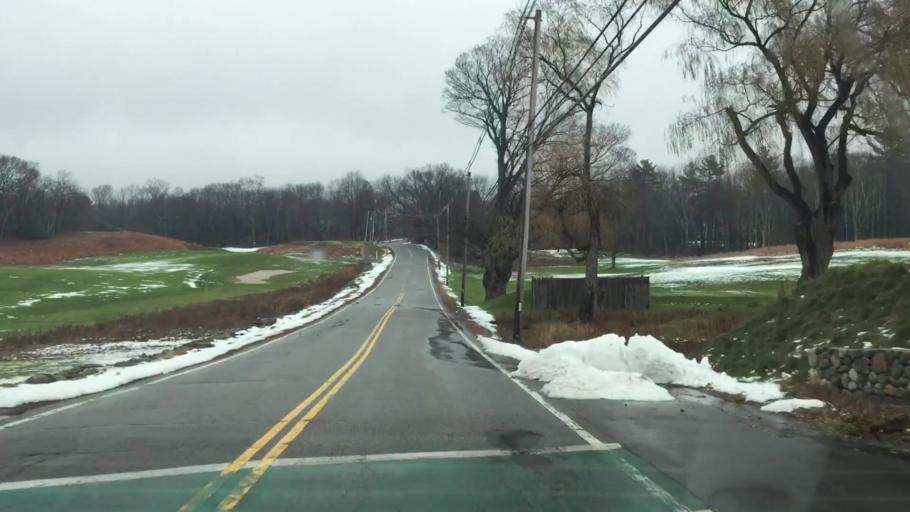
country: US
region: Massachusetts
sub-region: Essex County
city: North Andover
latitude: 42.6924
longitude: -71.0921
